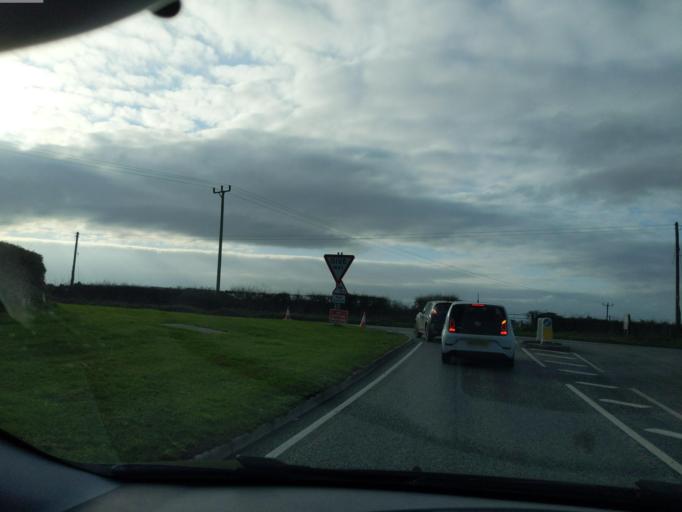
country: GB
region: England
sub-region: Cornwall
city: Padstow
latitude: 50.5137
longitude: -4.9484
